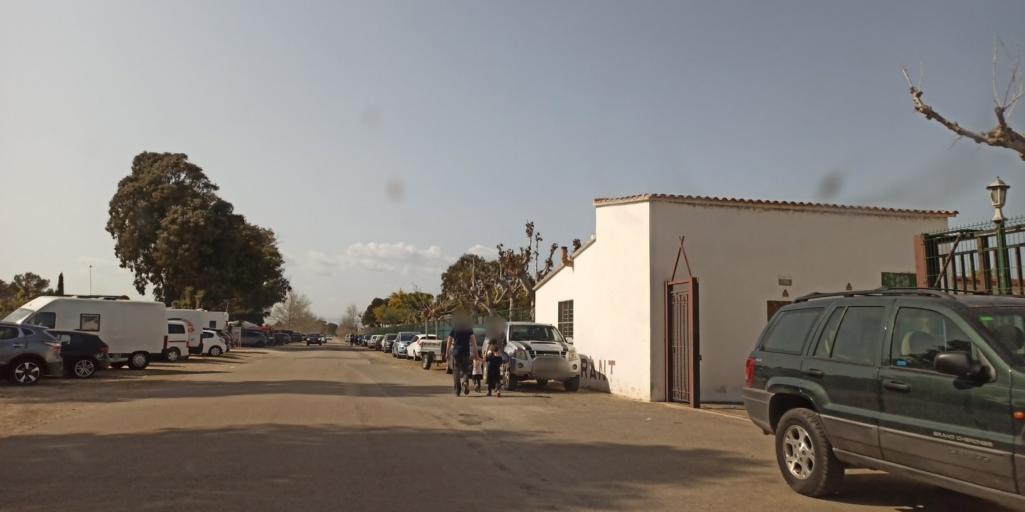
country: ES
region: Catalonia
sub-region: Provincia de Tarragona
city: Deltebre
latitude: 40.7201
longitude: 0.8486
